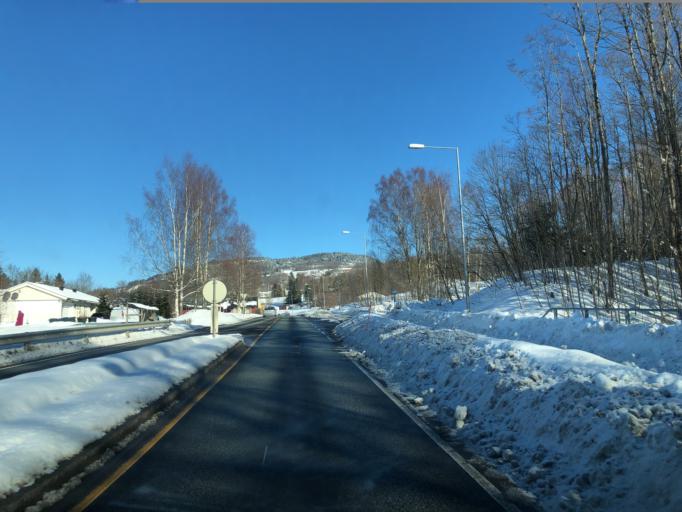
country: NO
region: Buskerud
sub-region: Lier
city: Tranby
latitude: 59.8169
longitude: 10.2491
